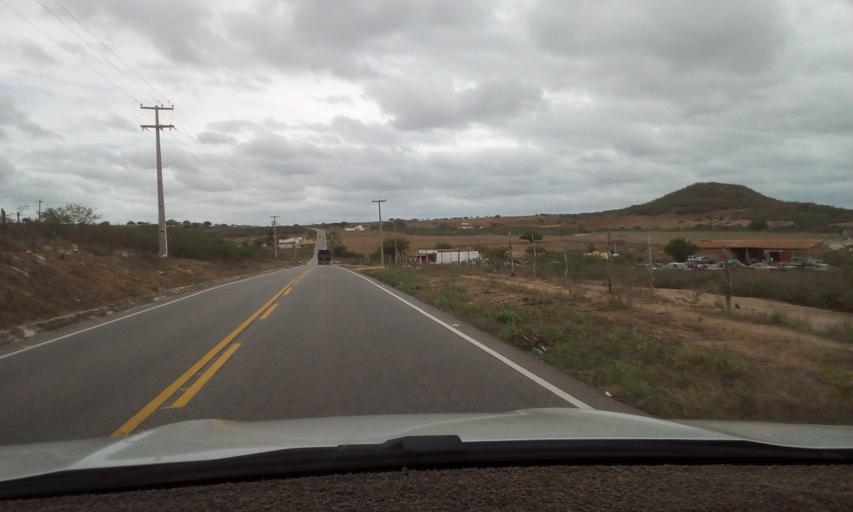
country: BR
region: Paraiba
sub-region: Picui
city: Picui
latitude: -6.5863
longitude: -36.2456
